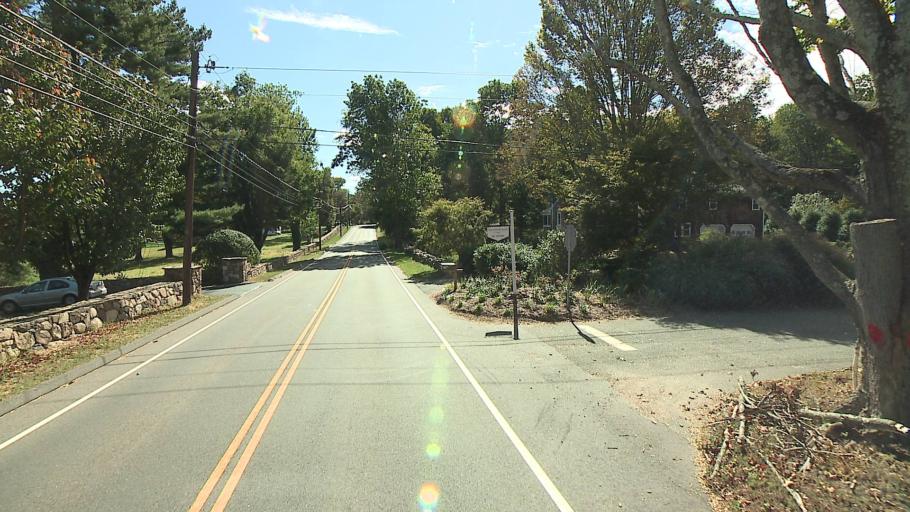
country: US
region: Connecticut
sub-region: Fairfield County
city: Wilton
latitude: 41.1985
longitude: -73.4073
